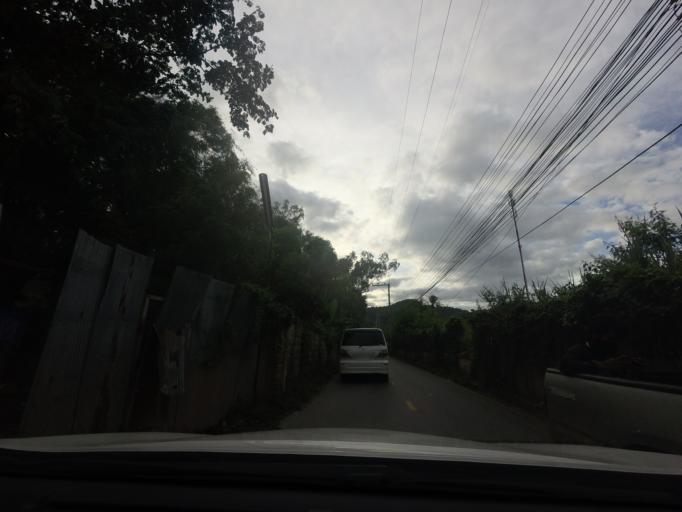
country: TH
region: Nakhon Ratchasima
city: Pak Chong
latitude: 14.6093
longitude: 101.4043
